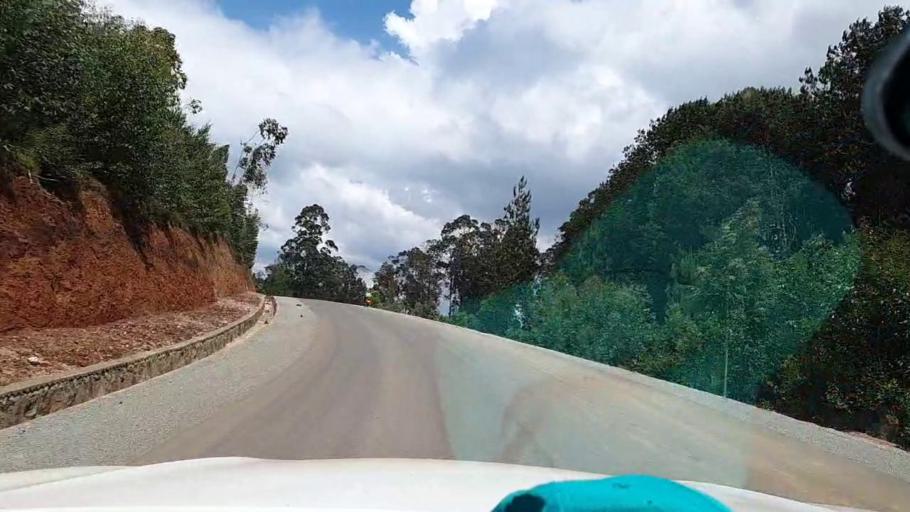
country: RW
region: Southern Province
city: Nzega
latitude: -2.6427
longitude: 29.5800
